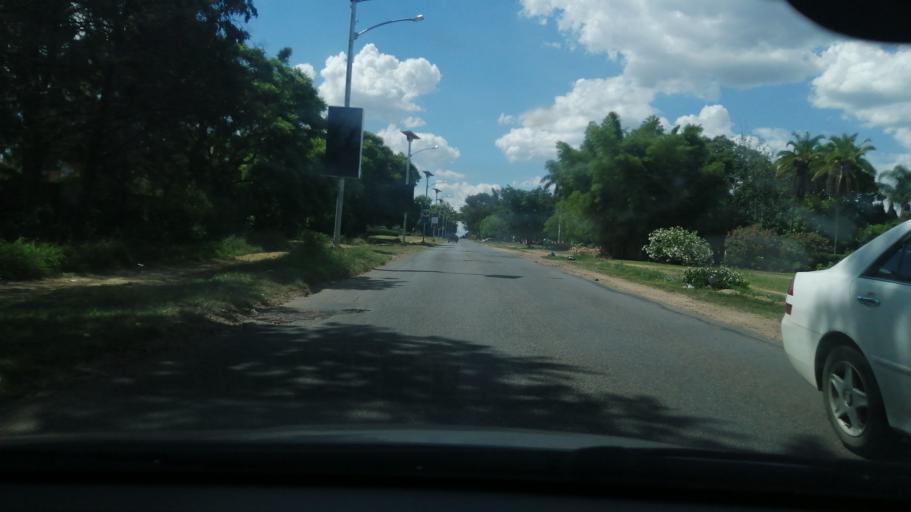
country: ZW
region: Harare
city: Harare
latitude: -17.7987
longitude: 31.0724
